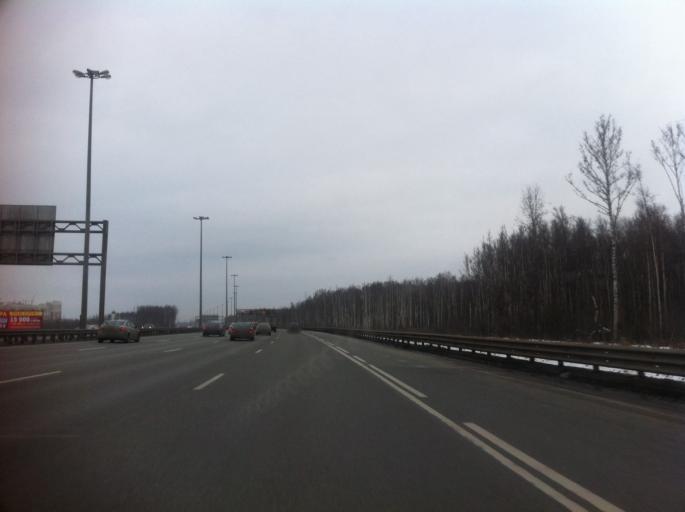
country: RU
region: Leningrad
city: Rybatskoye
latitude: 59.8904
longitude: 30.5243
